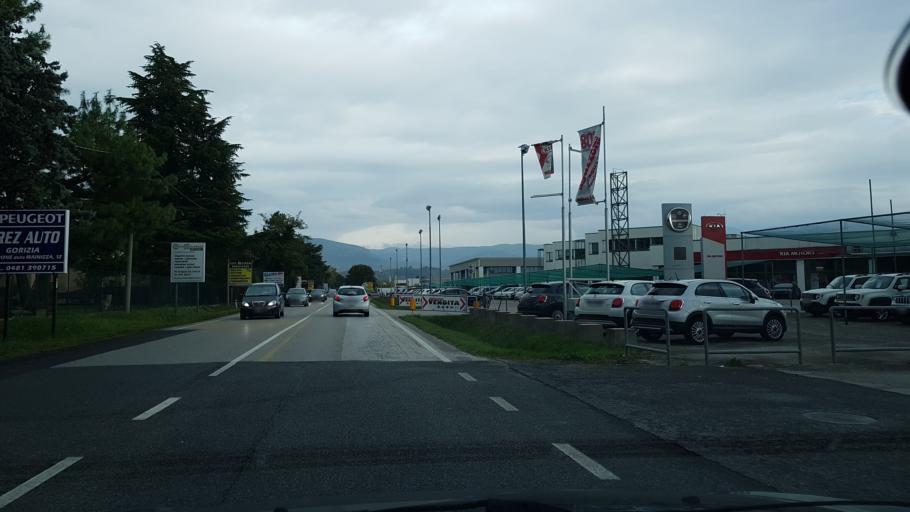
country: IT
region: Friuli Venezia Giulia
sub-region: Provincia di Gorizia
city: Gorizia
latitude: 45.9267
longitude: 13.6195
